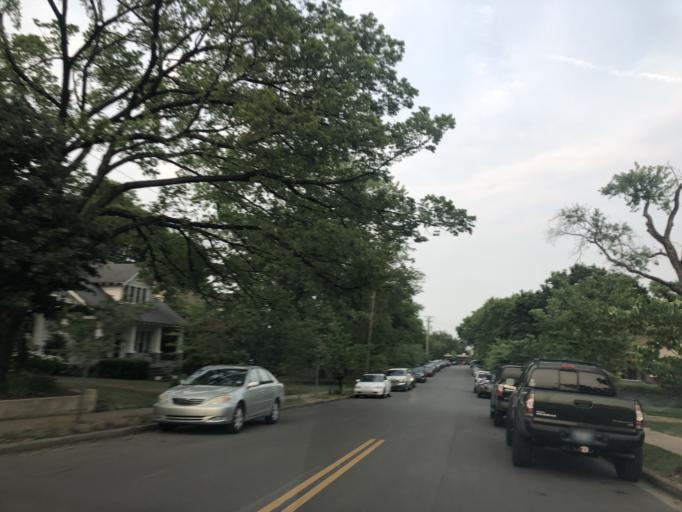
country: US
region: Tennessee
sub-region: Davidson County
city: Oak Hill
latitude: 36.1267
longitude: -86.7915
